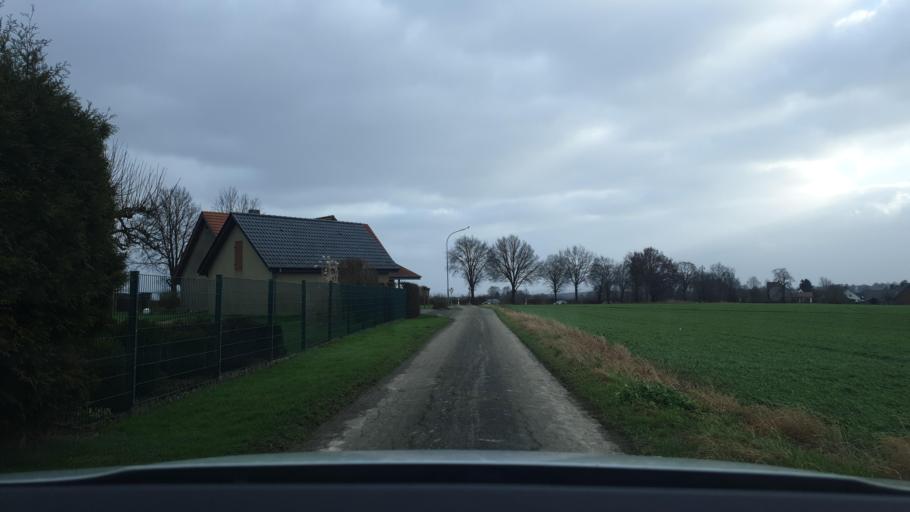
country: DE
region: North Rhine-Westphalia
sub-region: Regierungsbezirk Detmold
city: Huellhorst
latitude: 52.2547
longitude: 8.6337
